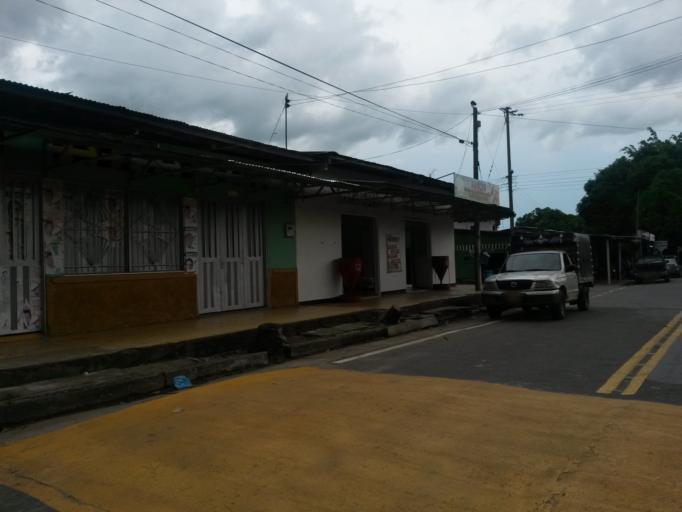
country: CO
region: Caqueta
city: Morelia
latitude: 1.4869
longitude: -75.7266
